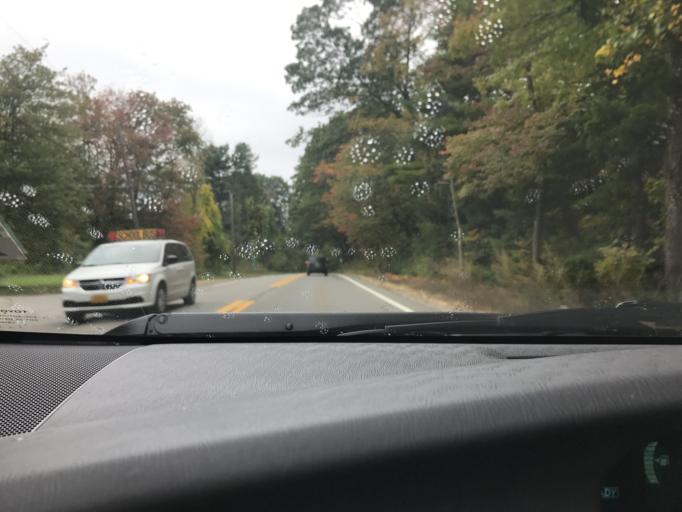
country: US
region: Massachusetts
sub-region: Middlesex County
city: Lincoln
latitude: 42.4522
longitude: -71.2996
